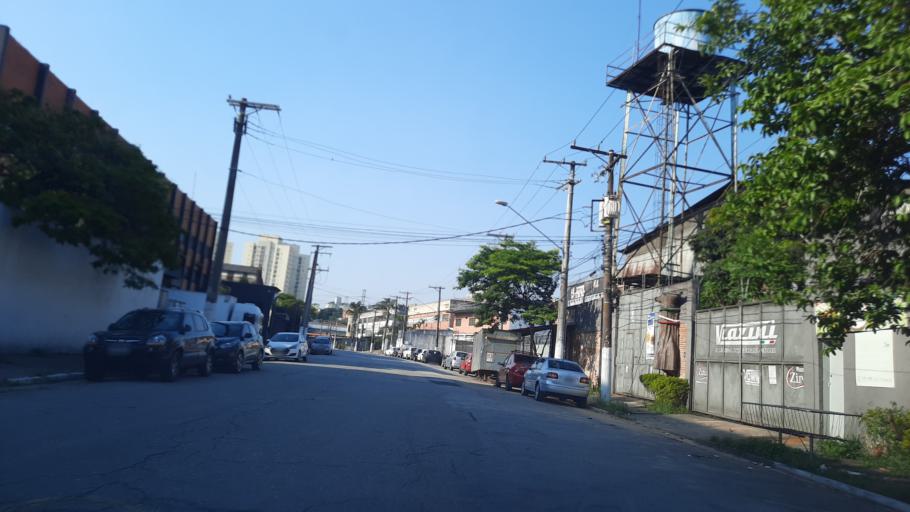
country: BR
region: Sao Paulo
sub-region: Sao Paulo
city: Sao Paulo
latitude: -23.5070
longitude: -46.6828
